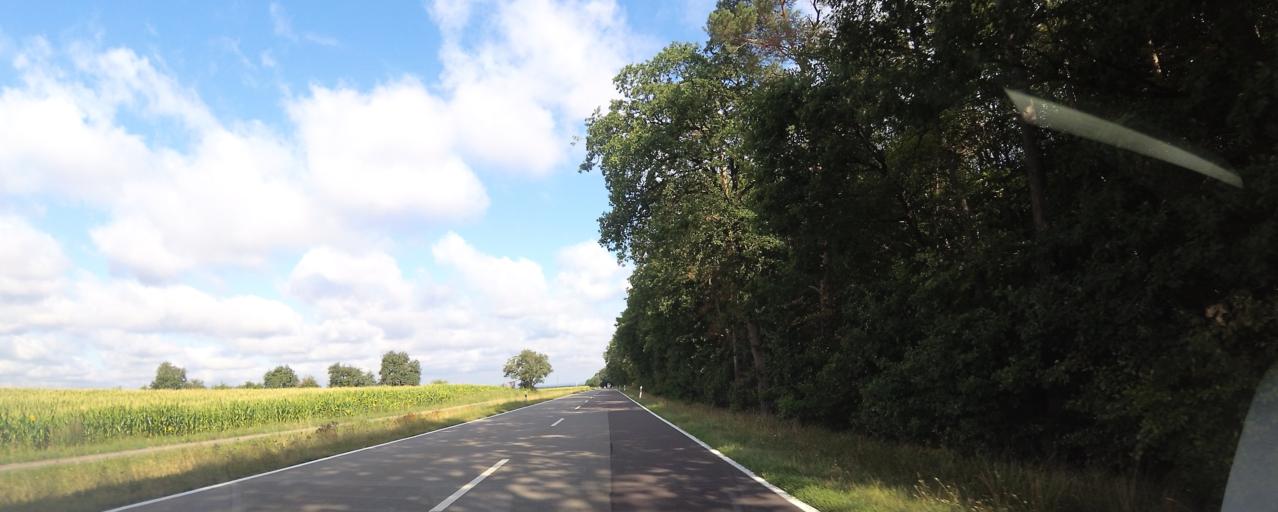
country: DE
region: Rheinland-Pfalz
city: Zemmer
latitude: 49.8887
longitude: 6.7134
